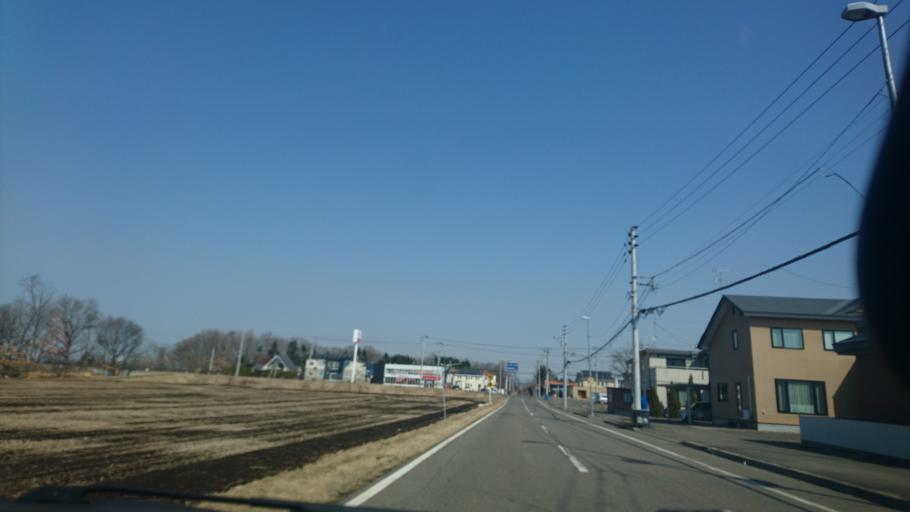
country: JP
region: Hokkaido
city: Obihiro
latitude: 42.9111
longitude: 143.0703
